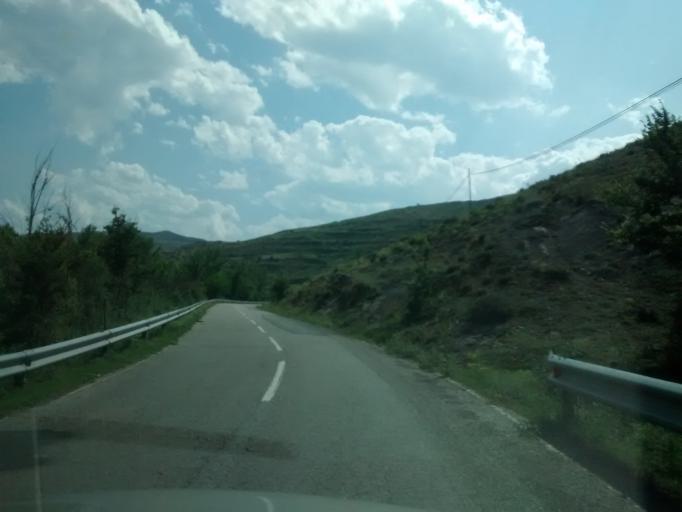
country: ES
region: La Rioja
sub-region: Provincia de La Rioja
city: San Roman de Cameros
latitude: 42.2278
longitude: -2.4794
